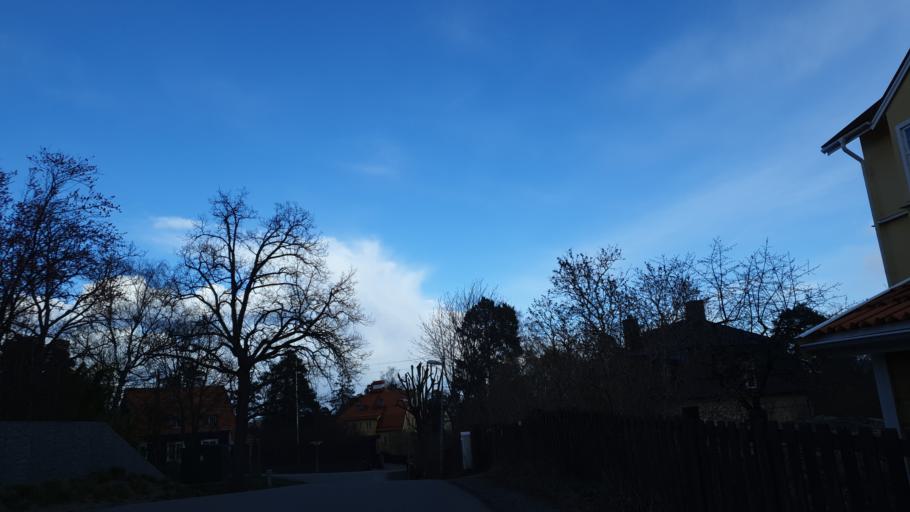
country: SE
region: Stockholm
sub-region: Lidingo
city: Lidingoe
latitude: 59.3687
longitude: 18.1346
